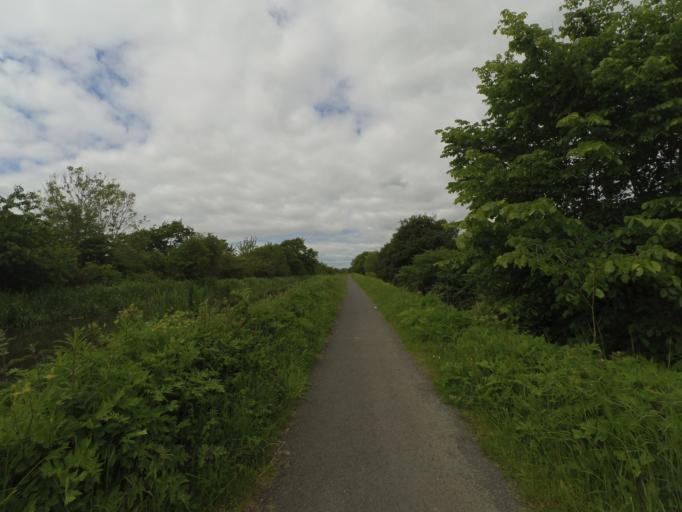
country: GB
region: Scotland
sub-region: Falkirk
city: Polmont
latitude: 55.9761
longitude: -3.6768
